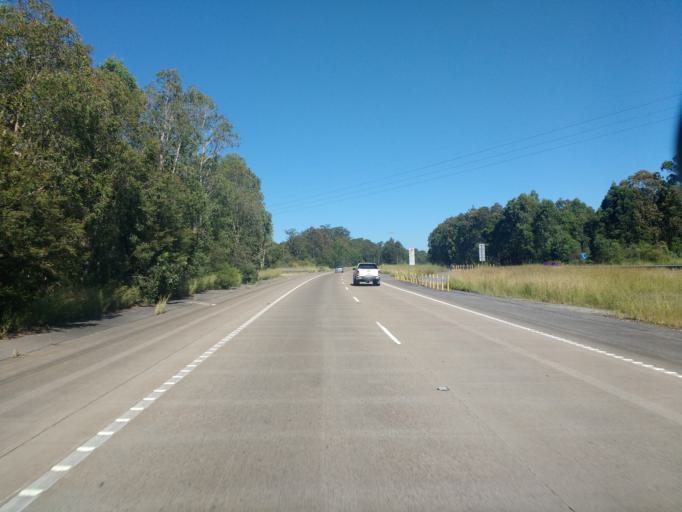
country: AU
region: New South Wales
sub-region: Lake Macquarie Shire
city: Holmesville
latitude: -32.8903
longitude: 151.6002
